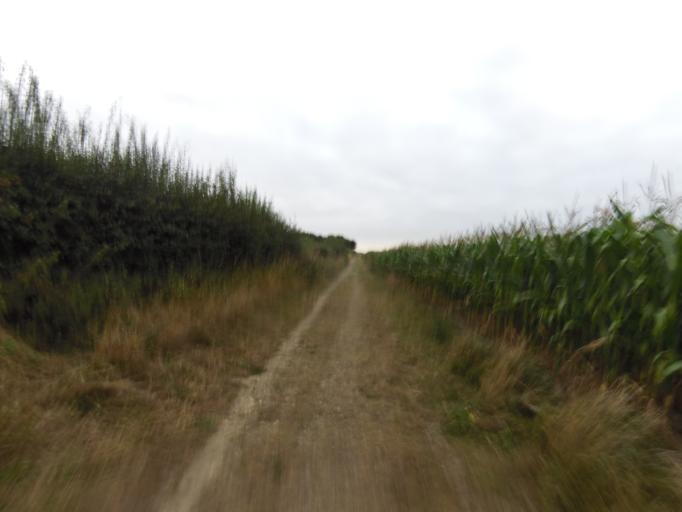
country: GB
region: England
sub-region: Hertfordshire
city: Radlett
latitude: 51.7186
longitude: -0.3161
